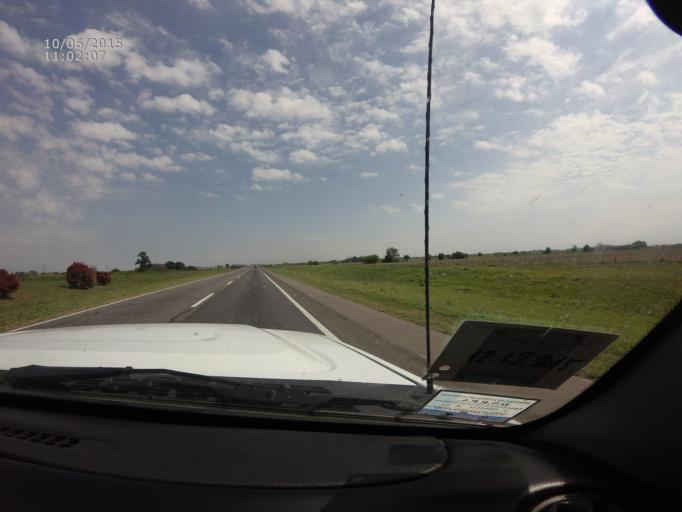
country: AR
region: Santa Fe
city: Villa Constitucion
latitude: -33.2517
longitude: -60.4262
